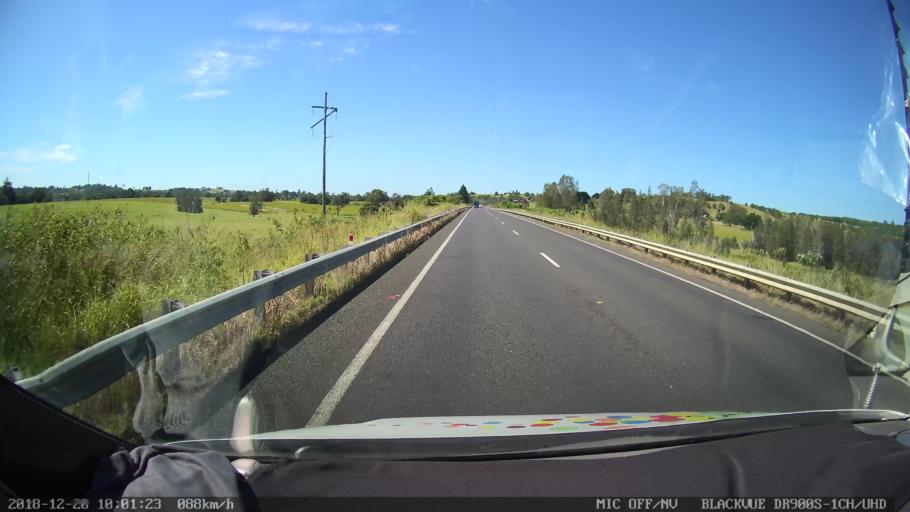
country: AU
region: New South Wales
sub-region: Lismore Municipality
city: Lismore
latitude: -28.8438
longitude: 153.2626
